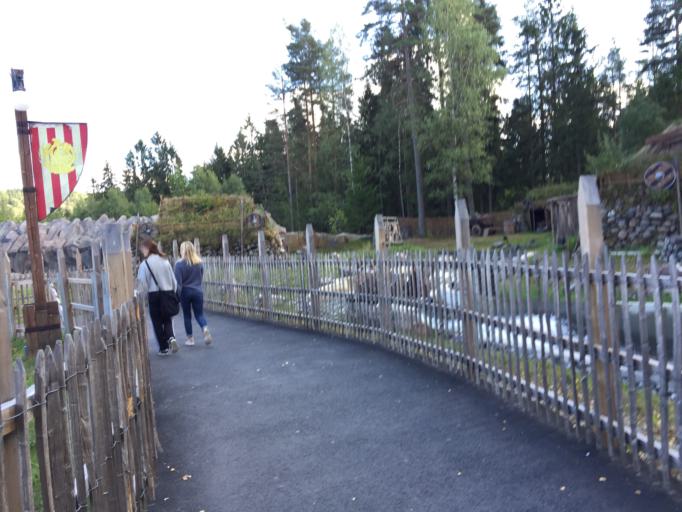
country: NO
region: Akershus
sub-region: Ski
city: Ski
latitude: 59.7447
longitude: 10.7779
